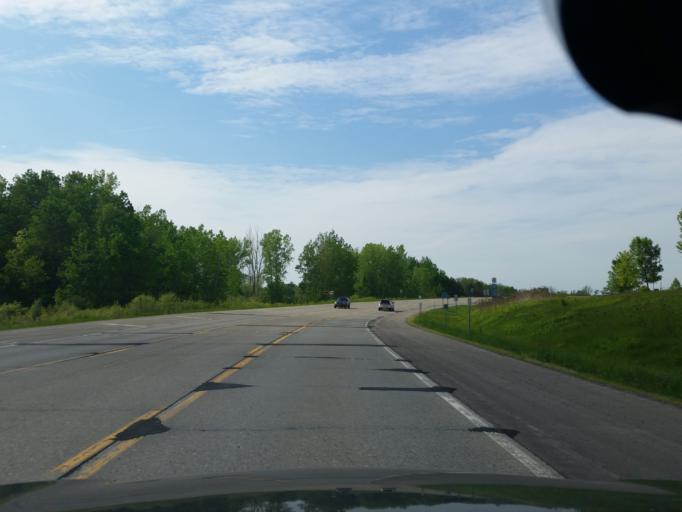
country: US
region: New York
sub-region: Chautauqua County
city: Lakewood
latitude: 42.1479
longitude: -79.4055
